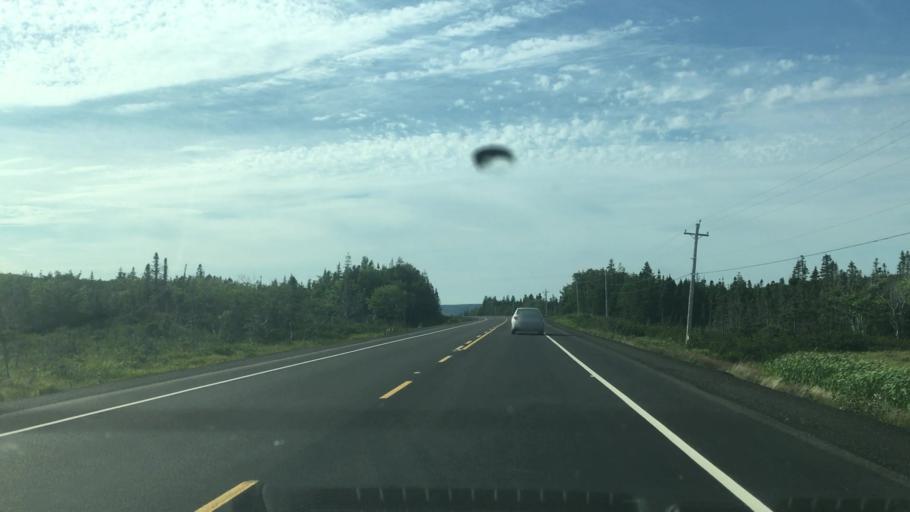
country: CA
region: Nova Scotia
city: Sydney Mines
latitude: 46.8477
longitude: -60.4145
